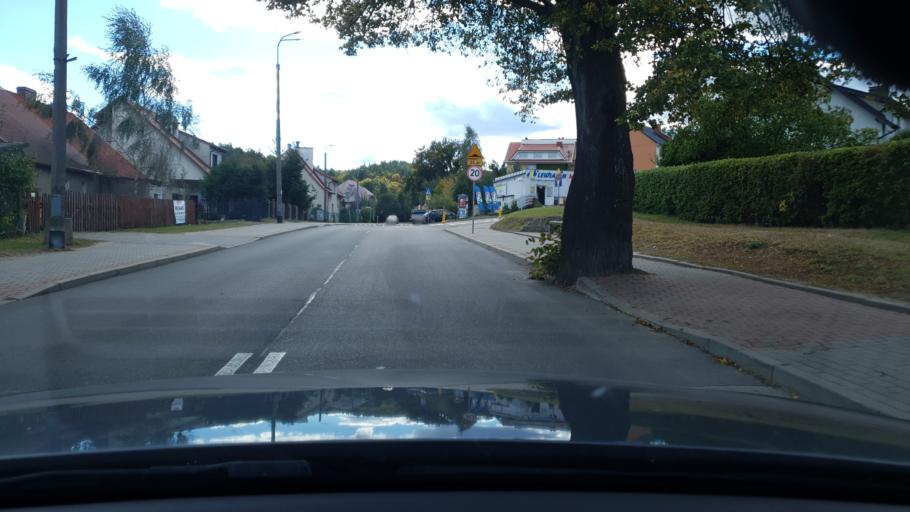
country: PL
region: Pomeranian Voivodeship
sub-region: Powiat wejherowski
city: Reda
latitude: 54.5986
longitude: 18.3465
